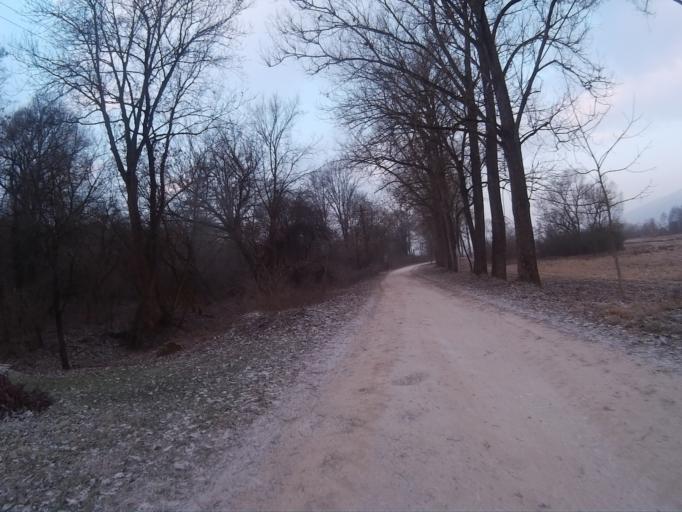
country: HU
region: Borsod-Abauj-Zemplen
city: Szendro
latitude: 48.5160
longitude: 20.7387
